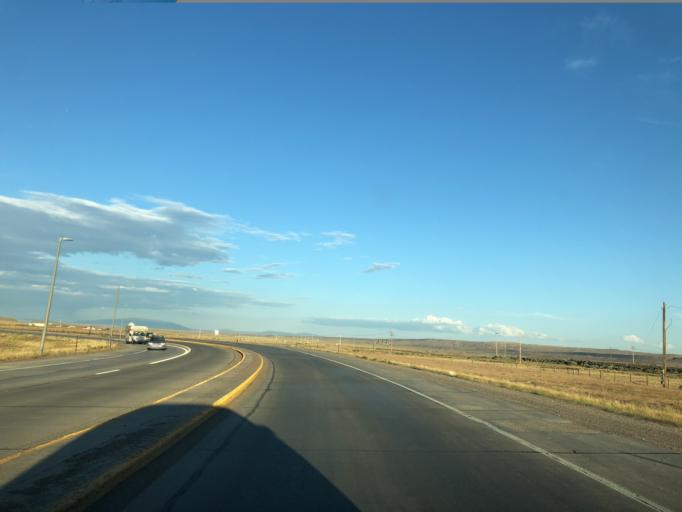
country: US
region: Wyoming
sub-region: Carbon County
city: Rawlins
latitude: 41.7879
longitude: -107.1988
